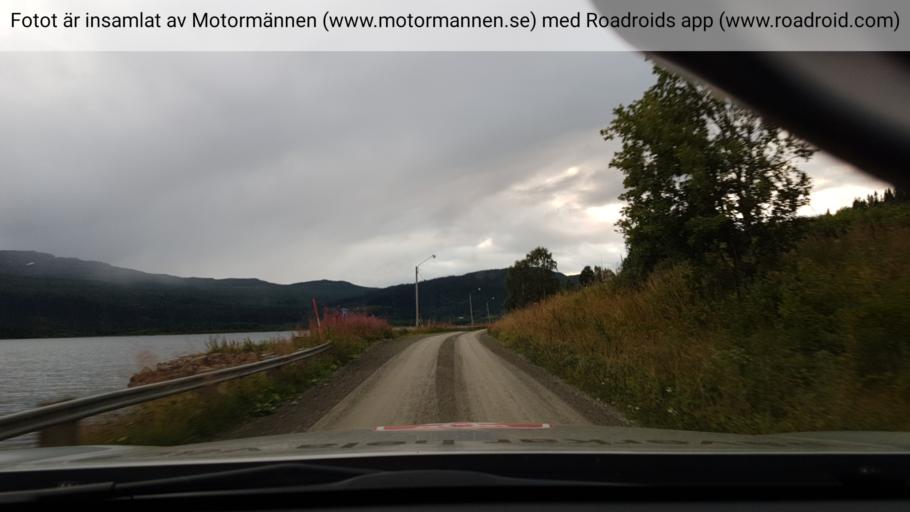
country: NO
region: Nordland
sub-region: Hattfjelldal
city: Hattfjelldal
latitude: 65.6516
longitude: 15.1738
